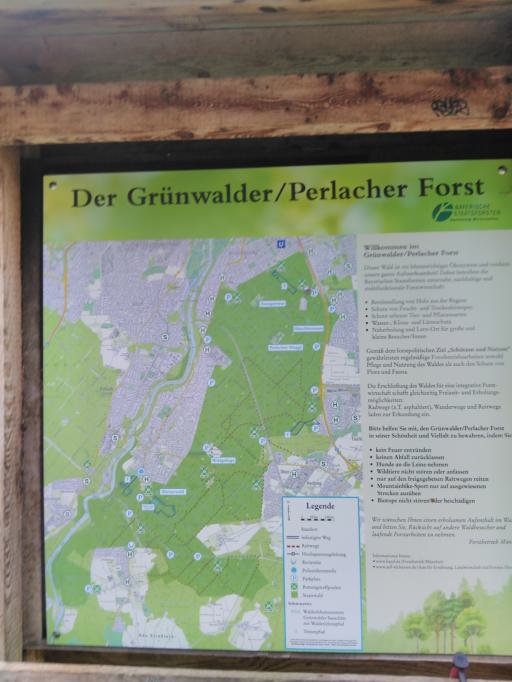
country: DE
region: Bavaria
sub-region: Upper Bavaria
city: Unterhaching
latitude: 48.0840
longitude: 11.5918
